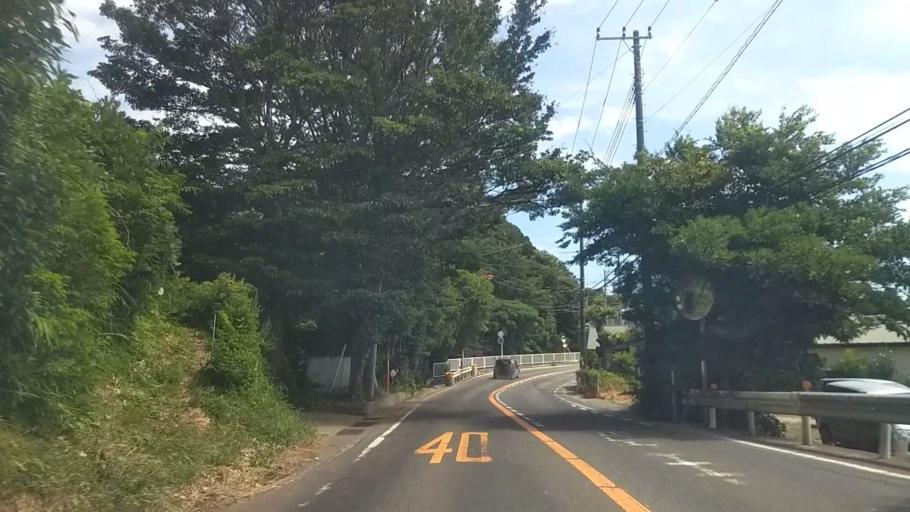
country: JP
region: Kanagawa
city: Miura
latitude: 35.2036
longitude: 139.6486
